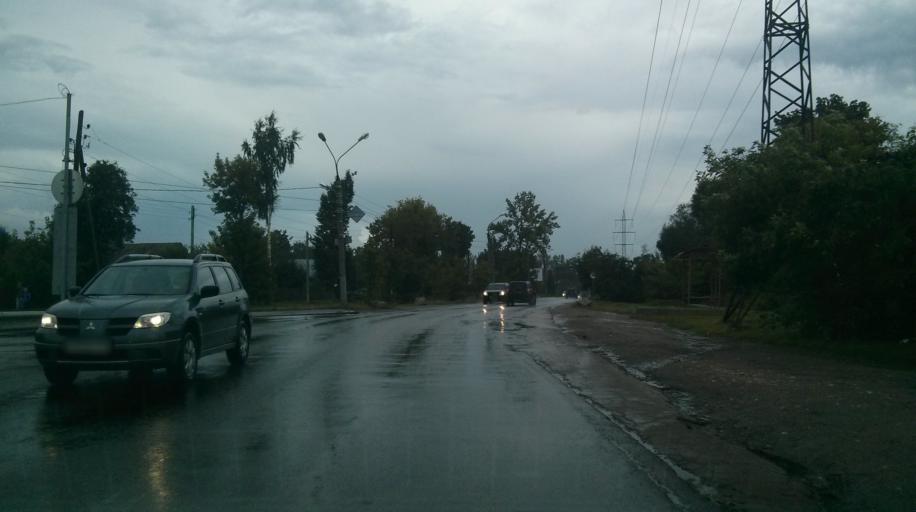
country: RU
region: Nizjnij Novgorod
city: Nizhniy Novgorod
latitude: 56.2580
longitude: 43.9991
